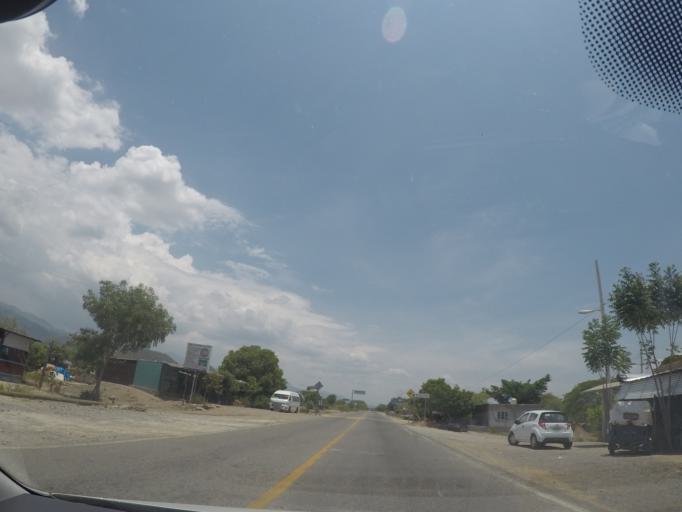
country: MX
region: Oaxaca
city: Santa Maria Jalapa del Marques
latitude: 16.4379
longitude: -95.5243
